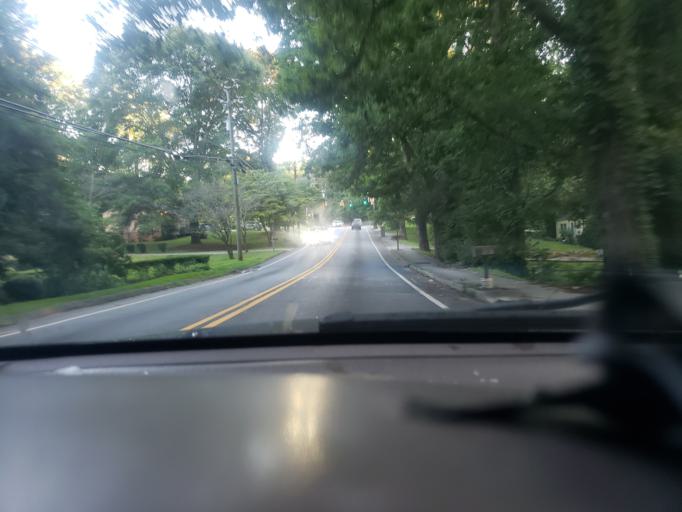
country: US
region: Georgia
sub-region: Fulton County
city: East Point
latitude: 33.7497
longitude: -84.5078
